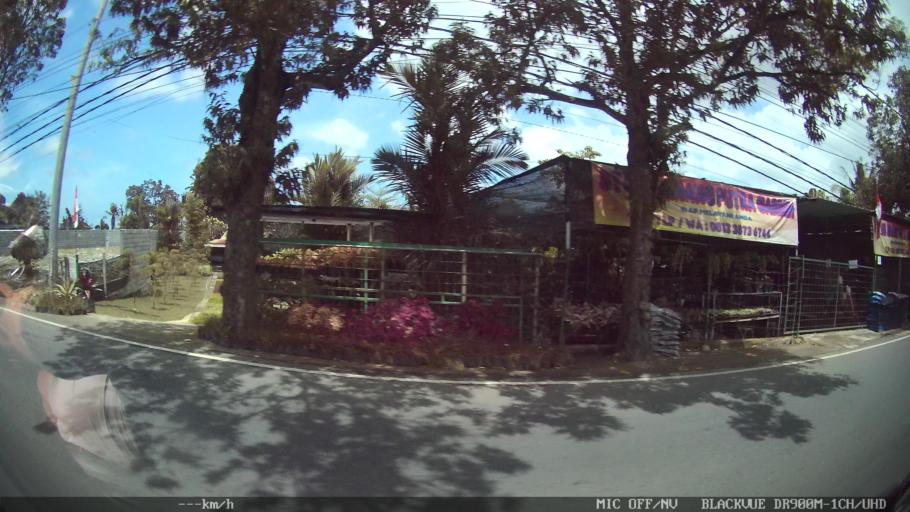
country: ID
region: Bali
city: Banjar Sedang
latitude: -8.5634
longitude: 115.2789
